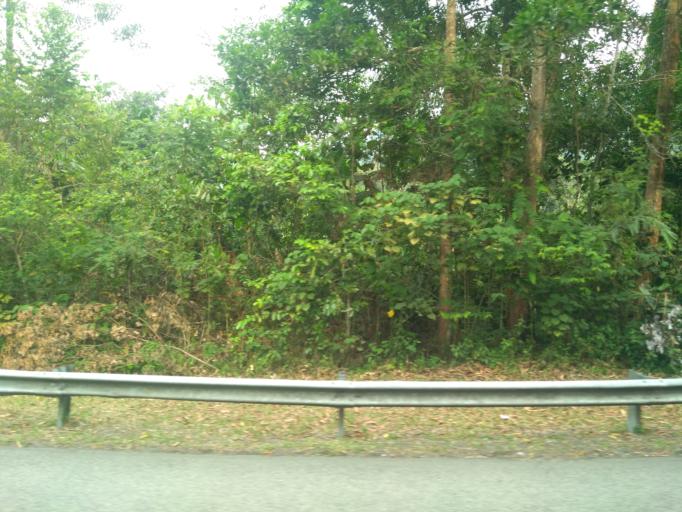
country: MY
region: Perak
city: Ipoh
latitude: 4.5719
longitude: 101.2480
